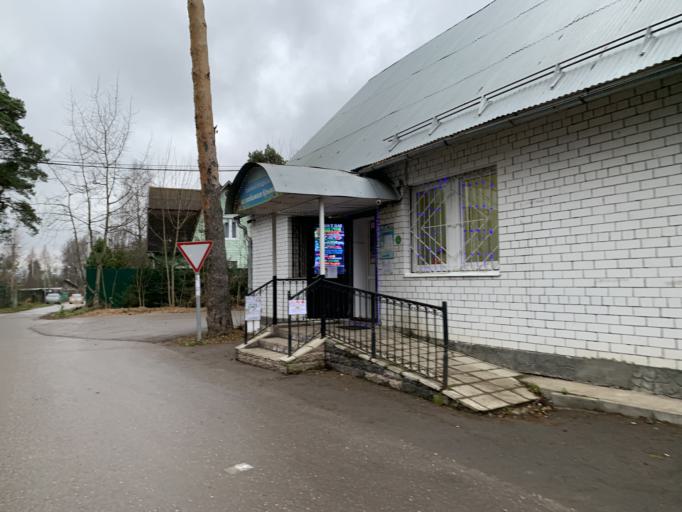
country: RU
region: Moskovskaya
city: Mamontovka
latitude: 55.9834
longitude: 37.8143
